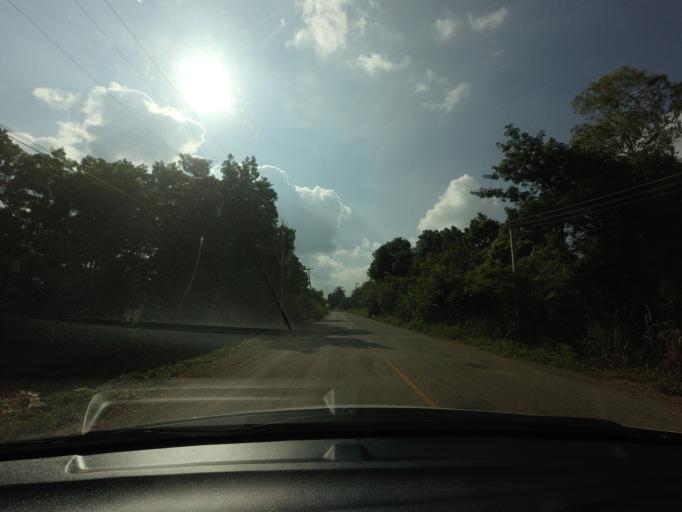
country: TH
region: Nakhon Ratchasima
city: Pak Chong
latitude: 14.5526
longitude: 101.6072
